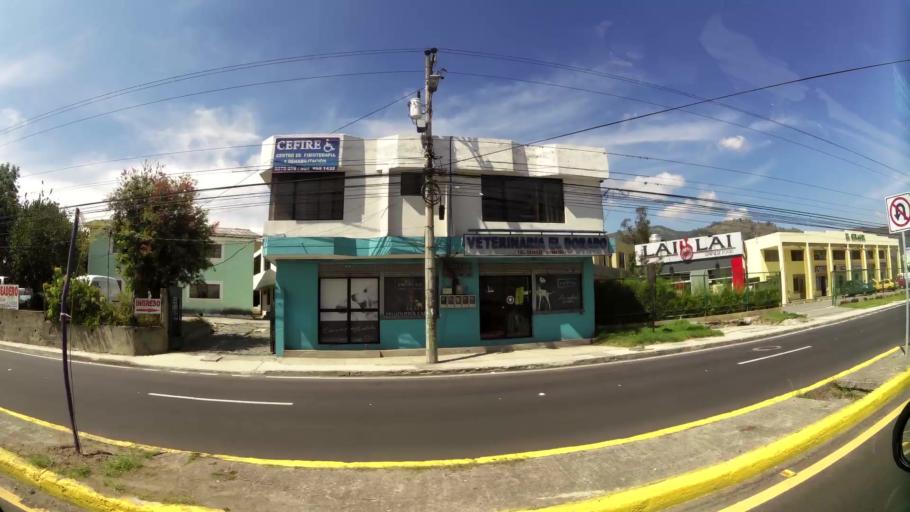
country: EC
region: Pichincha
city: Quito
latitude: -0.2170
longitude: -78.3982
